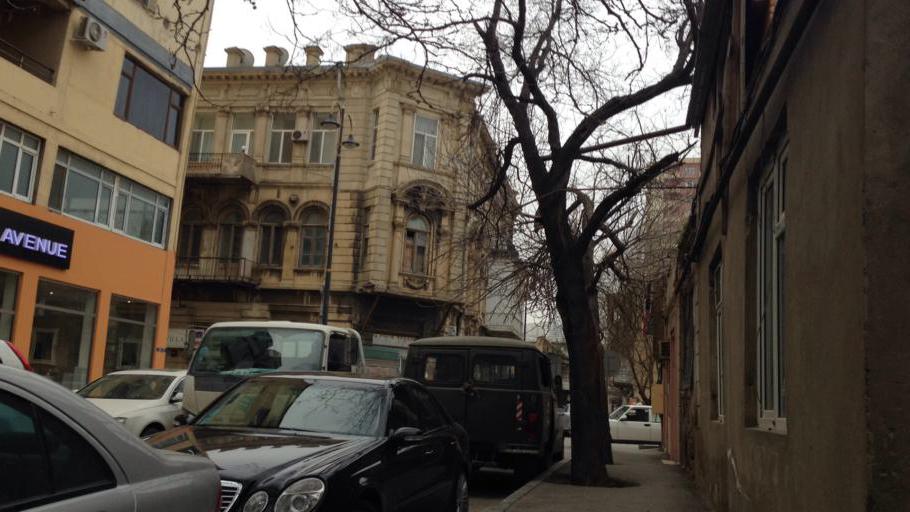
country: AZ
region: Baki
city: Badamdar
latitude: 40.3782
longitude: 49.8373
